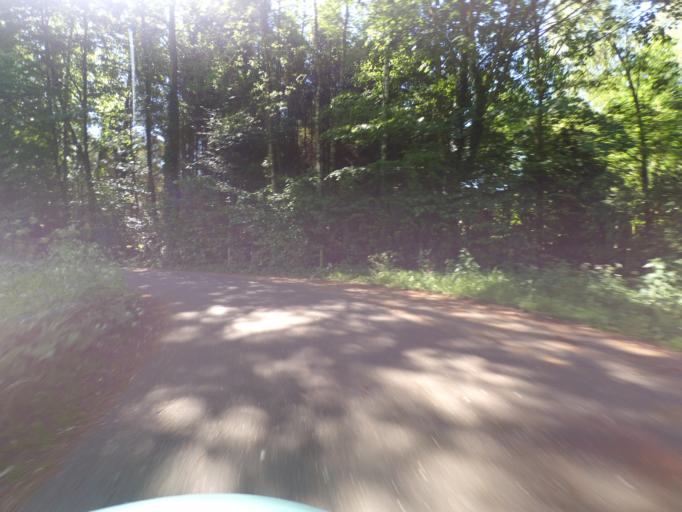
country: NL
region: Gelderland
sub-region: Gemeente Epe
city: Emst
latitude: 52.2979
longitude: 5.9982
